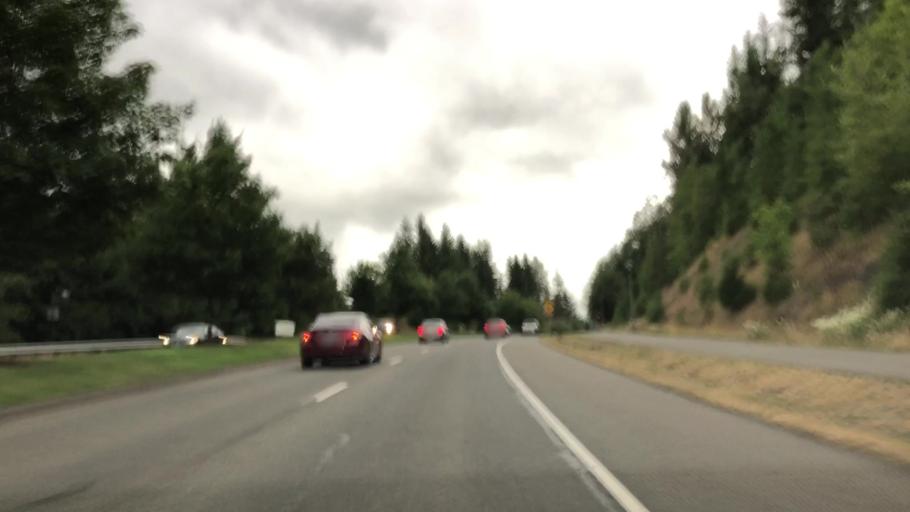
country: US
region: Washington
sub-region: King County
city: Fall City
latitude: 47.5190
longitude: -121.8791
